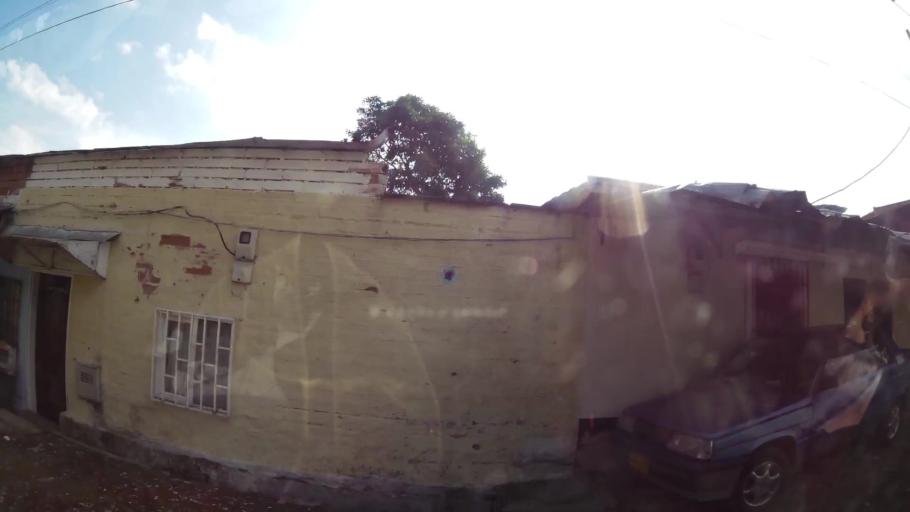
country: CO
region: Antioquia
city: La Estrella
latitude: 6.1706
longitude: -75.6434
